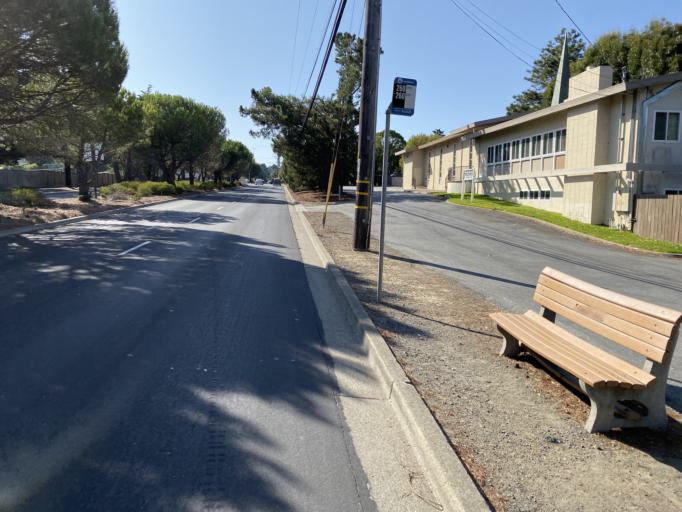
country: US
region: California
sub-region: San Mateo County
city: Highlands-Baywood Park
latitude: 37.5120
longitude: -122.3163
